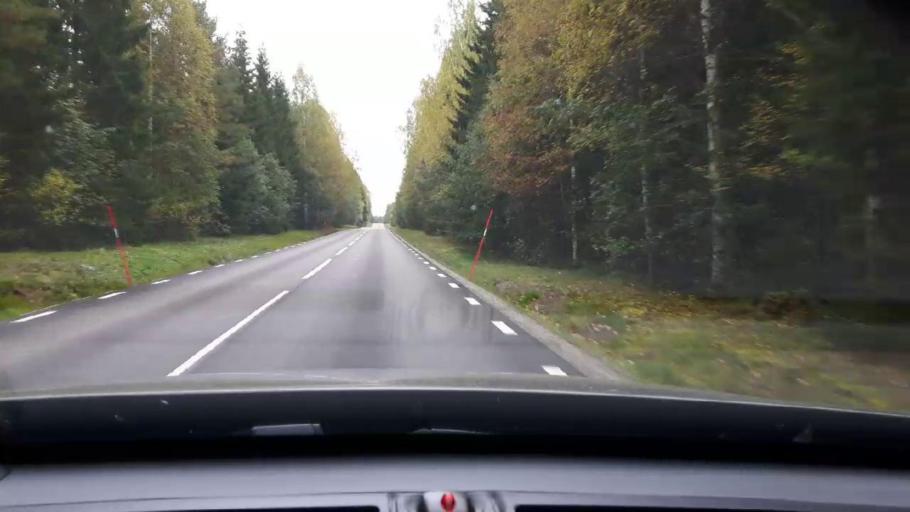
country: SE
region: Dalarna
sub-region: Ludvika Kommun
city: Grangesberg
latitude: 60.2315
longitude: 15.0357
